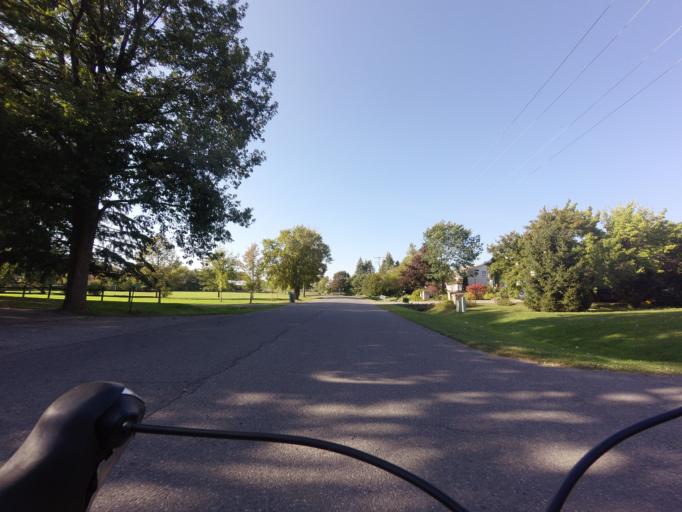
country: CA
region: Ontario
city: Bells Corners
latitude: 45.2272
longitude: -75.6772
